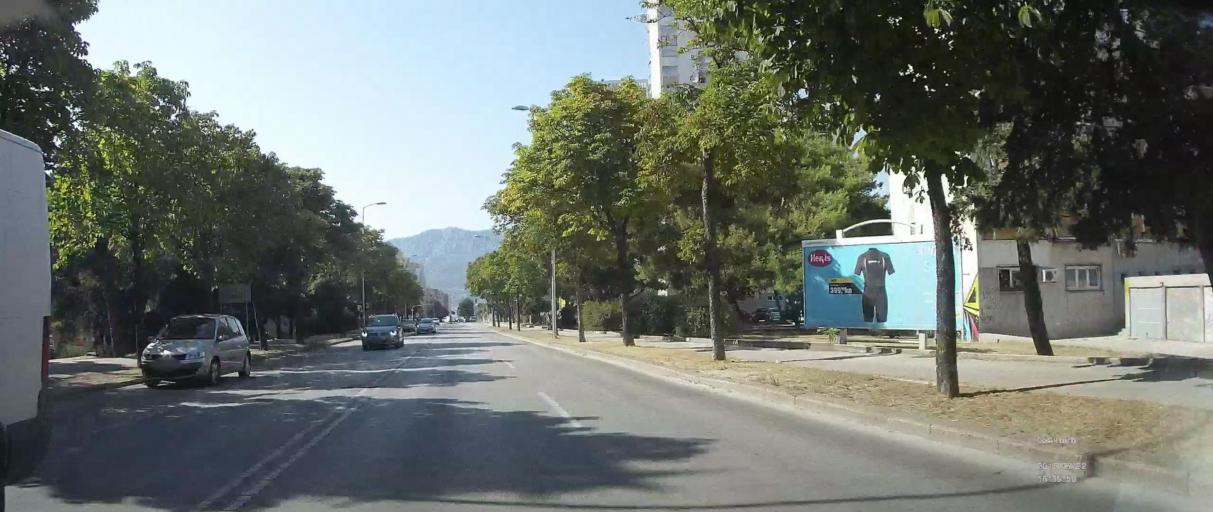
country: HR
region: Splitsko-Dalmatinska
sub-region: Grad Split
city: Split
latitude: 43.5141
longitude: 16.4532
